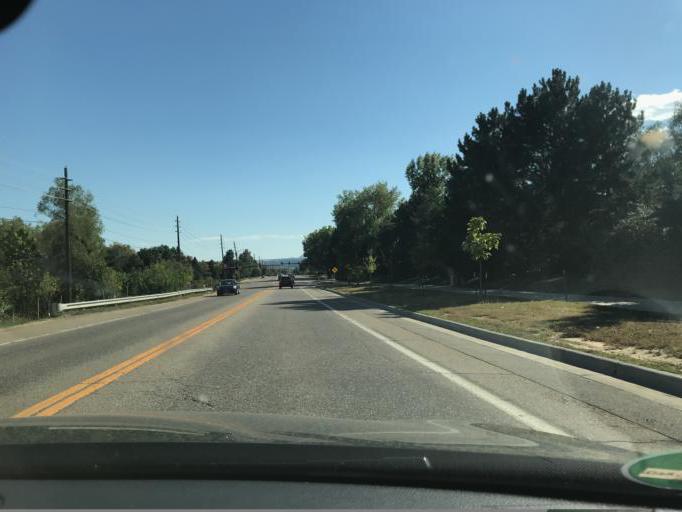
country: US
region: Colorado
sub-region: Boulder County
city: Boulder
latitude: 40.0419
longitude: -105.2585
